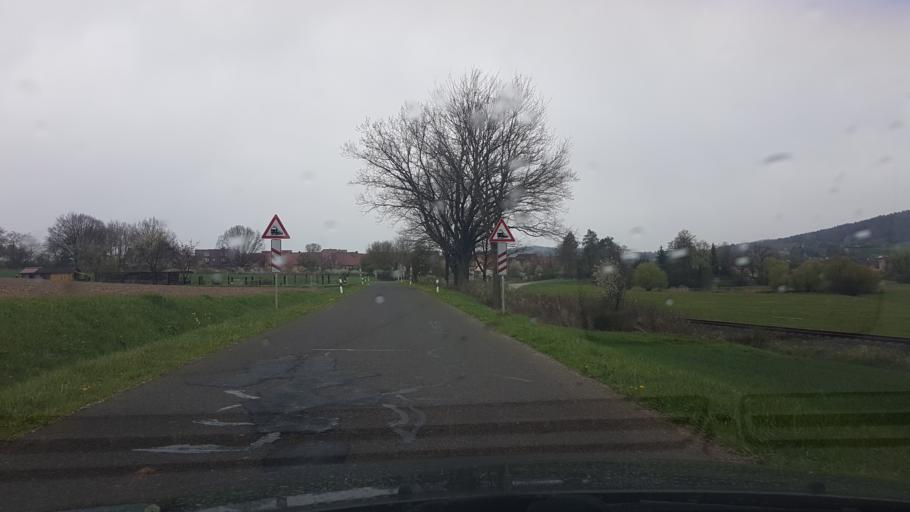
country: DE
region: Bavaria
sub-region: Upper Franconia
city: Reckendorf
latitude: 50.0238
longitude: 10.8386
